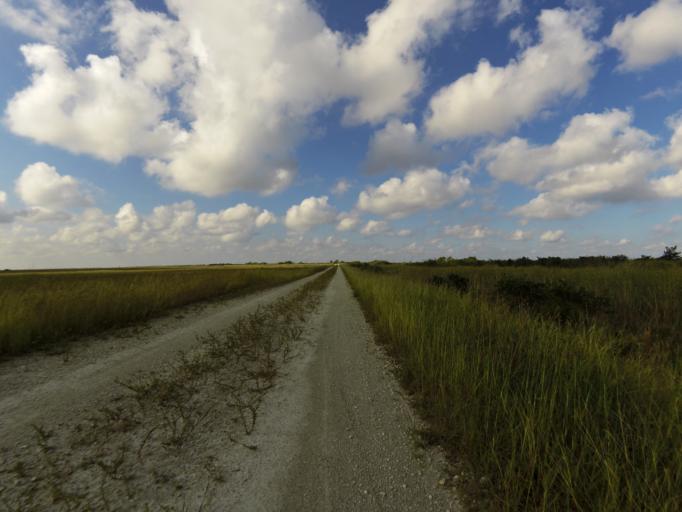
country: US
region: Florida
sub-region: Broward County
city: Weston
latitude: 26.0481
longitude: -80.4799
